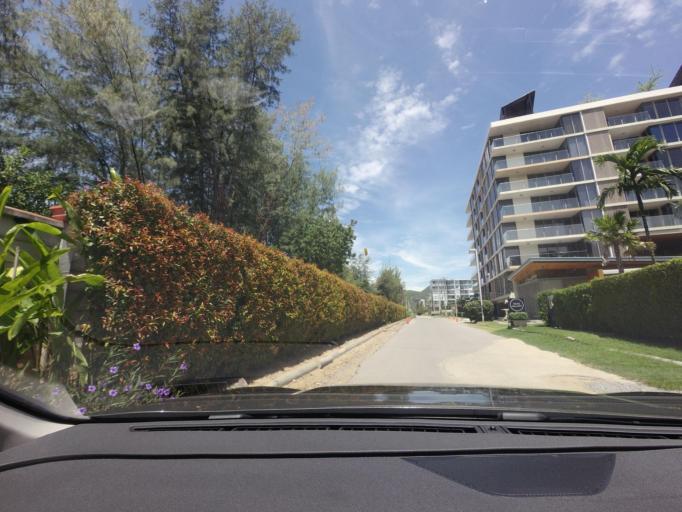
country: TH
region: Prachuap Khiri Khan
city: Hua Hin
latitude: 12.5104
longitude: 99.9762
